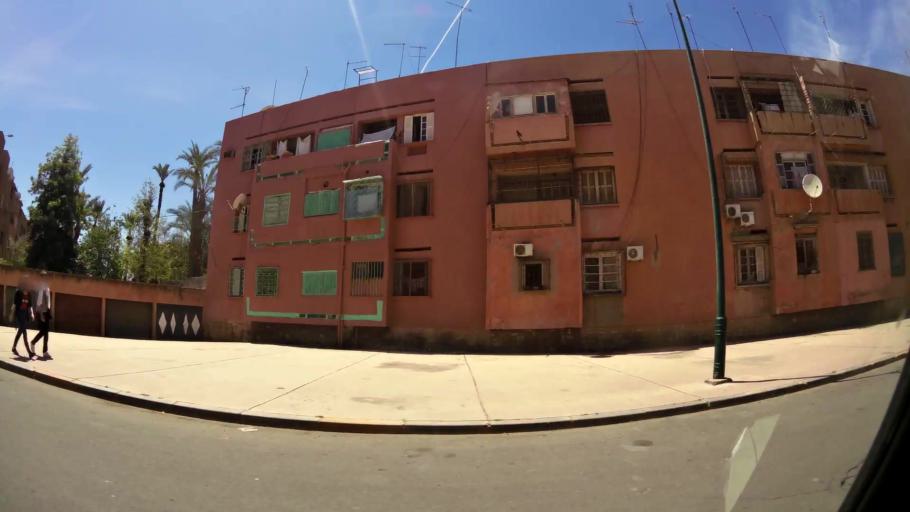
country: MA
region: Marrakech-Tensift-Al Haouz
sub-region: Marrakech
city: Marrakesh
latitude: 31.6316
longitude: -8.0019
